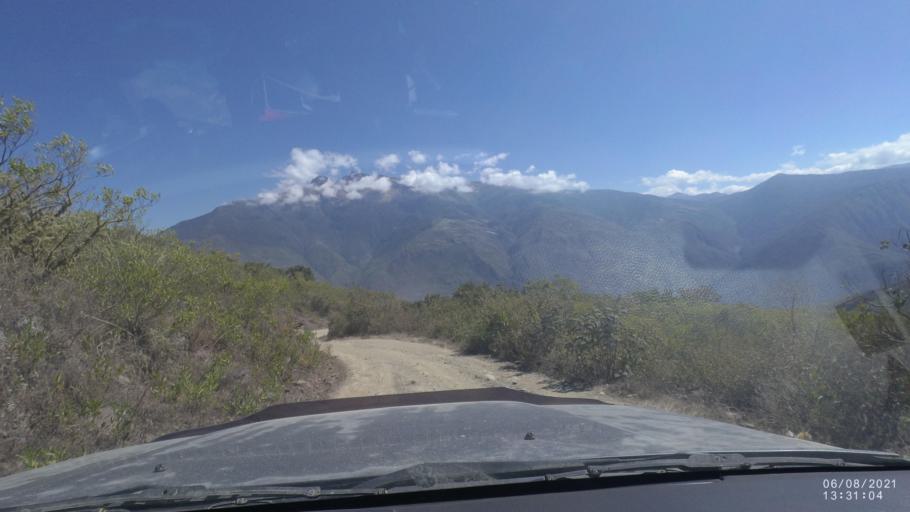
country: BO
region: La Paz
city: Quime
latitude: -16.7007
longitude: -66.7258
